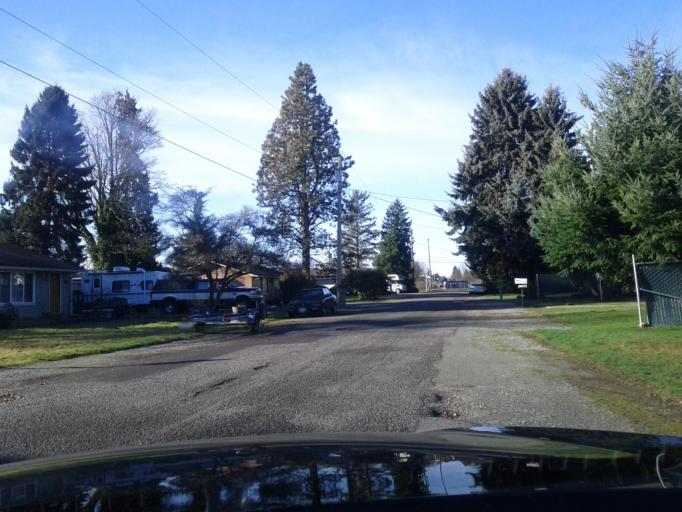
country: US
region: Washington
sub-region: Skagit County
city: Burlington
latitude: 48.4612
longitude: -122.3228
